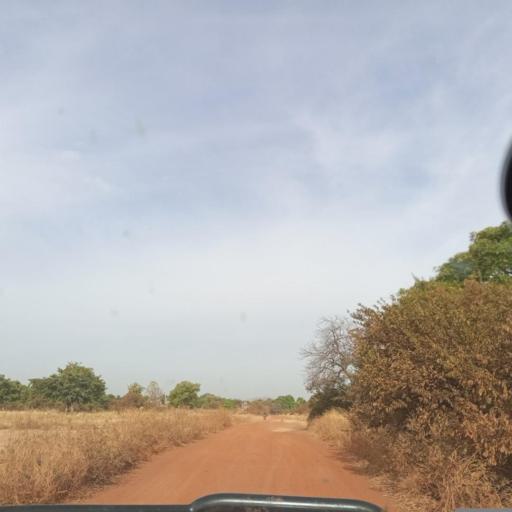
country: ML
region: Koulikoro
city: Koulikoro
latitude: 13.1069
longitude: -7.6466
